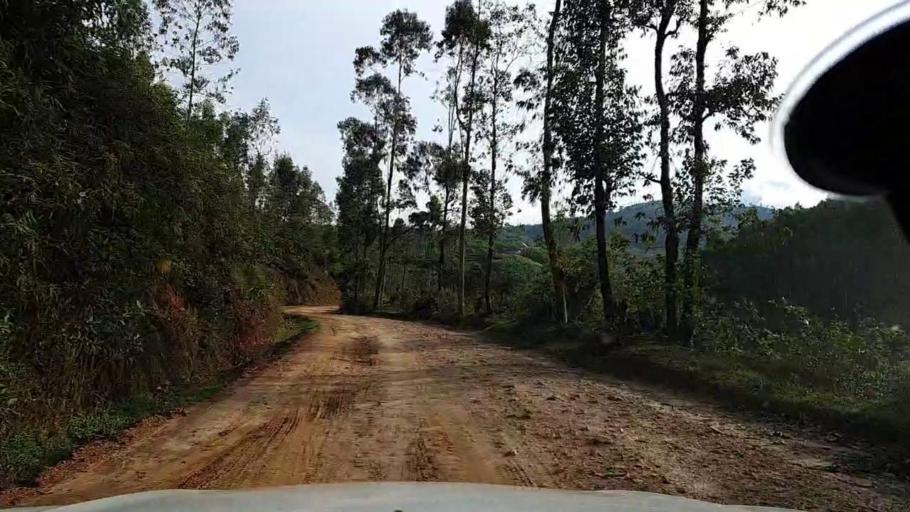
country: RW
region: Southern Province
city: Gitarama
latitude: -2.1696
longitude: 29.5542
